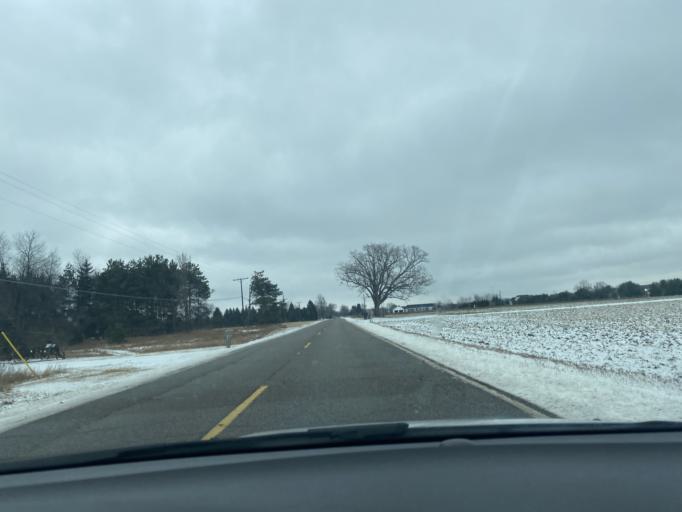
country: US
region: Michigan
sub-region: Lapeer County
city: Barnes Lake-Millers Lake
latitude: 43.2062
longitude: -83.2649
